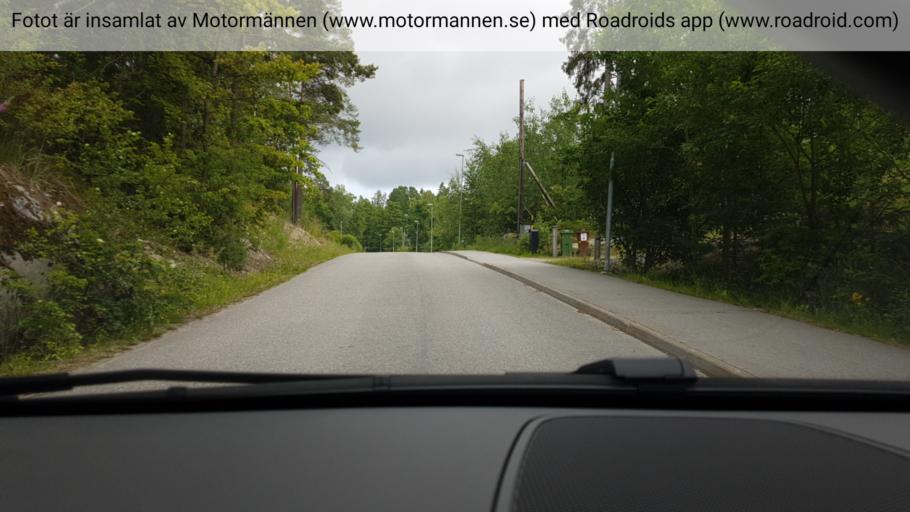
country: SE
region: Stockholm
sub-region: Nacka Kommun
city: Fisksatra
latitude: 59.2509
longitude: 18.2765
